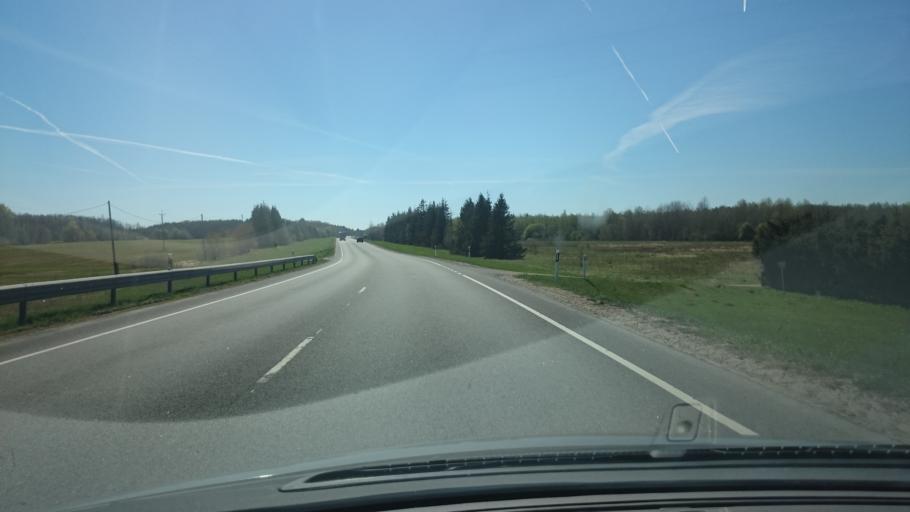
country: EE
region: Ida-Virumaa
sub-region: Narva-Joesuu linn
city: Narva-Joesuu
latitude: 59.3848
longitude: 27.9701
